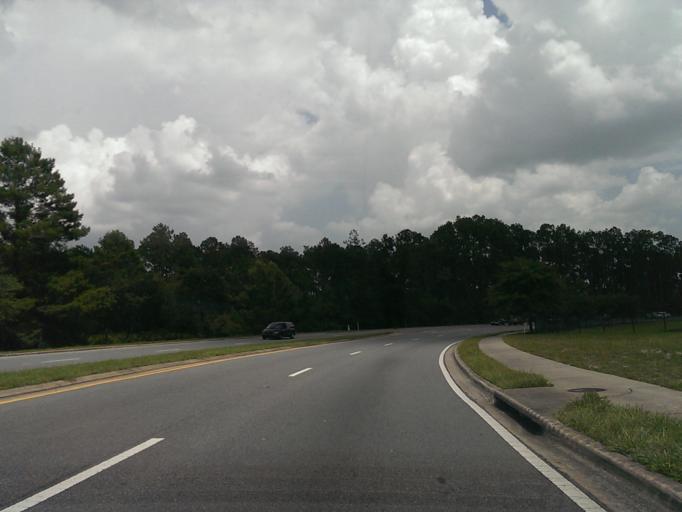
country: US
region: Florida
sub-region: Orange County
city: Doctor Phillips
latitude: 28.3985
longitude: -81.5207
